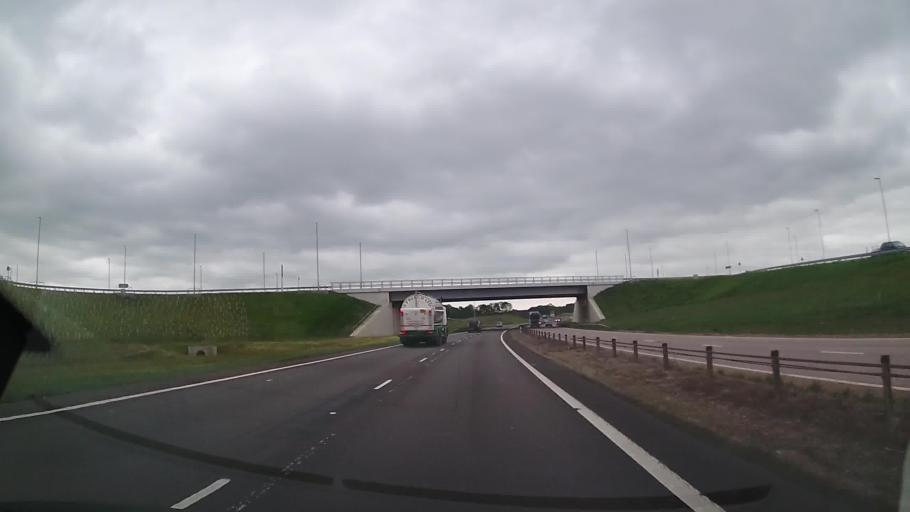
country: GB
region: England
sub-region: Staffordshire
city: Uttoxeter
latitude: 52.9137
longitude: -1.8951
